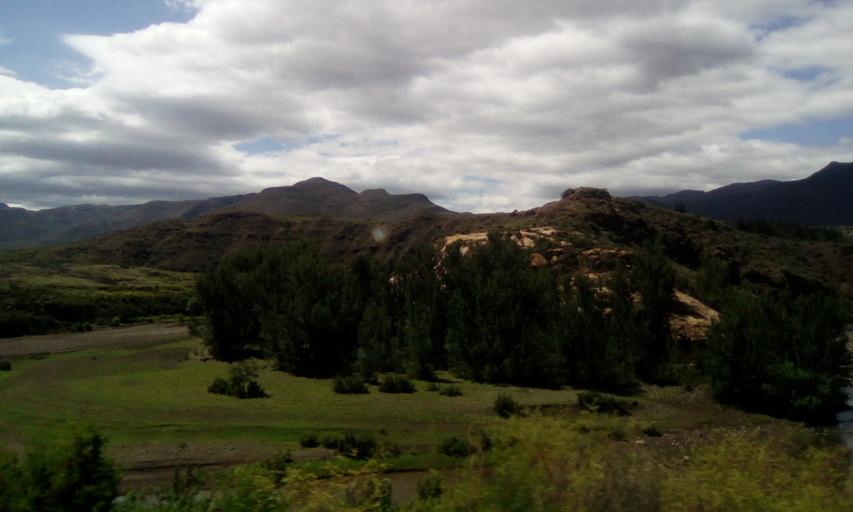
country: LS
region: Maseru
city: Nako
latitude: -29.6635
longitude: 27.8010
